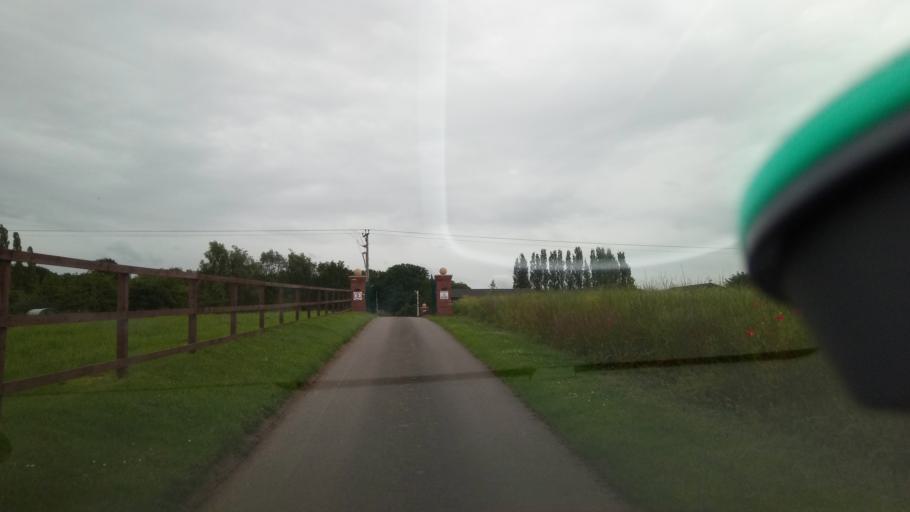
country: GB
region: England
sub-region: Derbyshire
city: Melbourne
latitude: 52.8452
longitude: -1.4166
